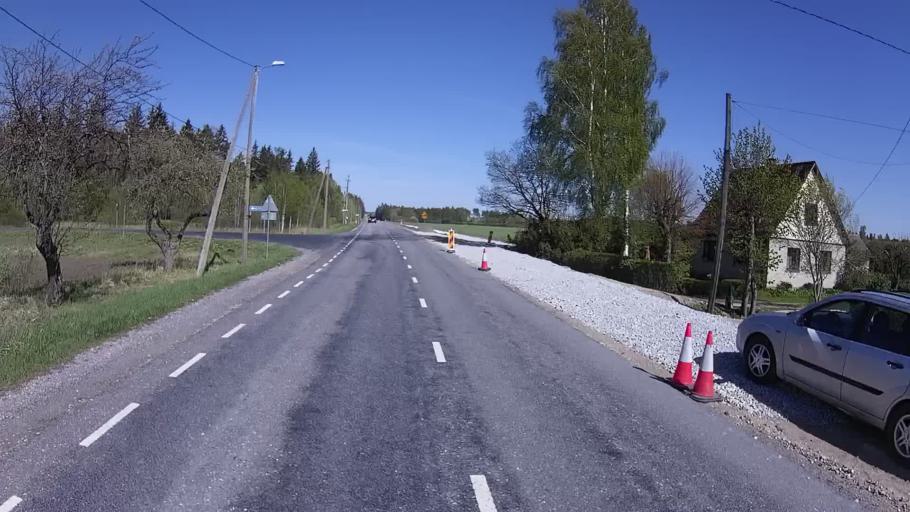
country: EE
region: Paernumaa
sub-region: Tootsi vald
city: Tootsi
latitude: 58.4891
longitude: 24.8107
